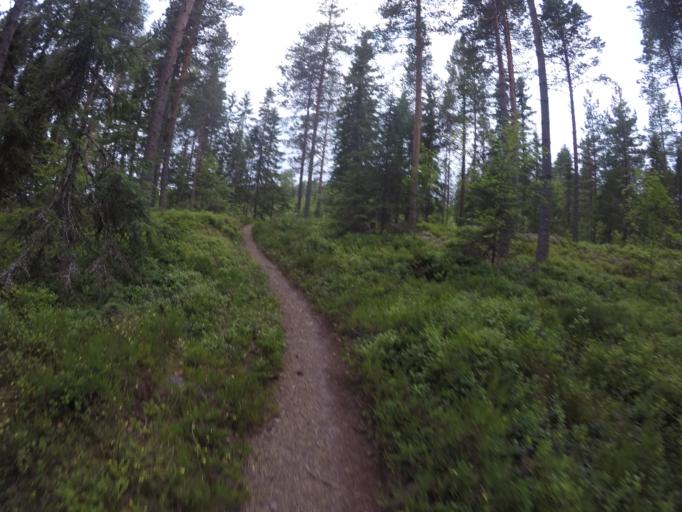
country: SE
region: Vaermland
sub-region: Filipstads Kommun
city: Lesjofors
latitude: 60.1575
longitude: 14.3971
